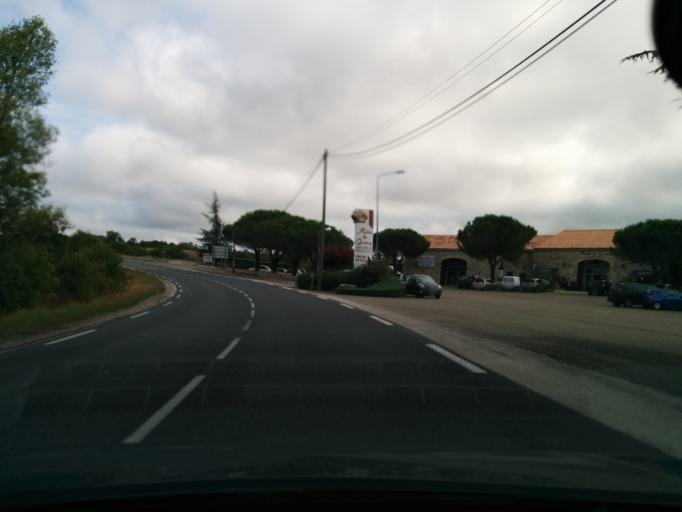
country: FR
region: Midi-Pyrenees
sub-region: Departement du Lot
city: Pradines
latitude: 44.5422
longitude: 1.4763
